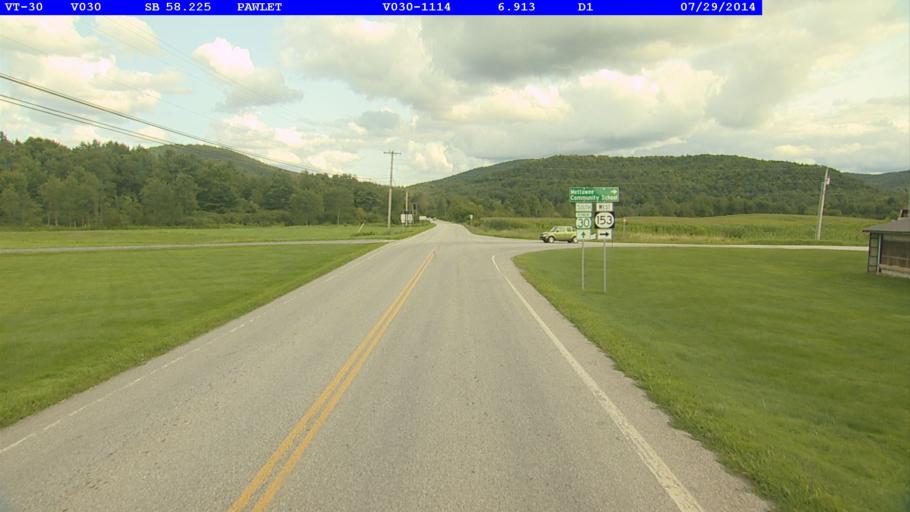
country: US
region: New York
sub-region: Washington County
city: Granville
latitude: 43.3895
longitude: -73.2204
